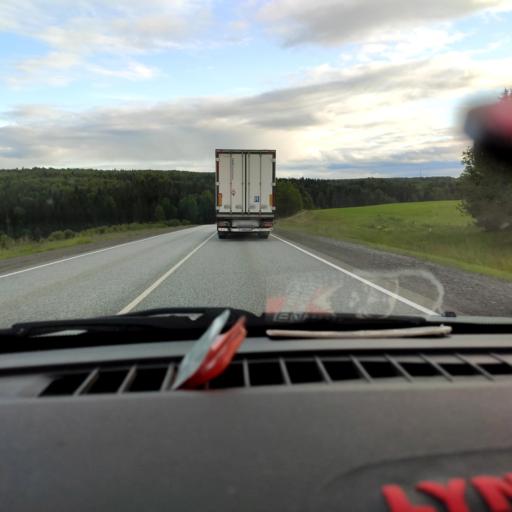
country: RU
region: Perm
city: Pavlovskiy
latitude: 57.9021
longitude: 54.9524
